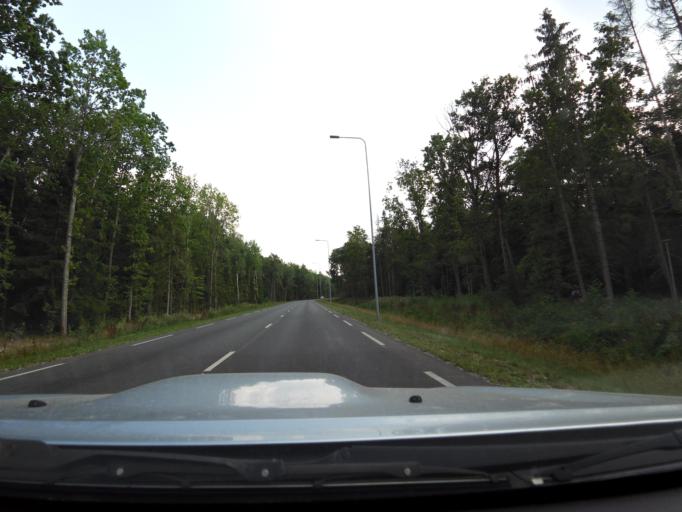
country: LT
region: Klaipedos apskritis
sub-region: Klaipeda
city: Klaipeda
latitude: 55.7531
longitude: 21.0904
